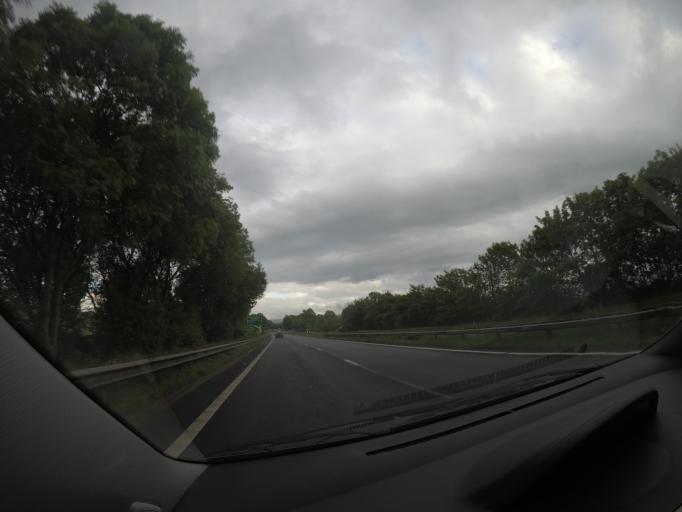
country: GB
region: England
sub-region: Cumbria
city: Kirkby Stephen
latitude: 54.5283
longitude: -2.3291
